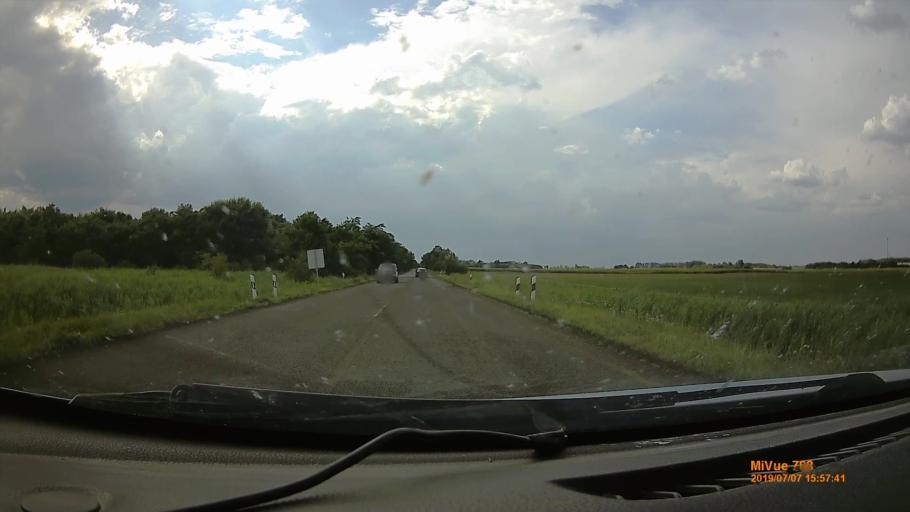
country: HU
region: Pest
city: Szentlorinckata
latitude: 47.5778
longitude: 19.7587
